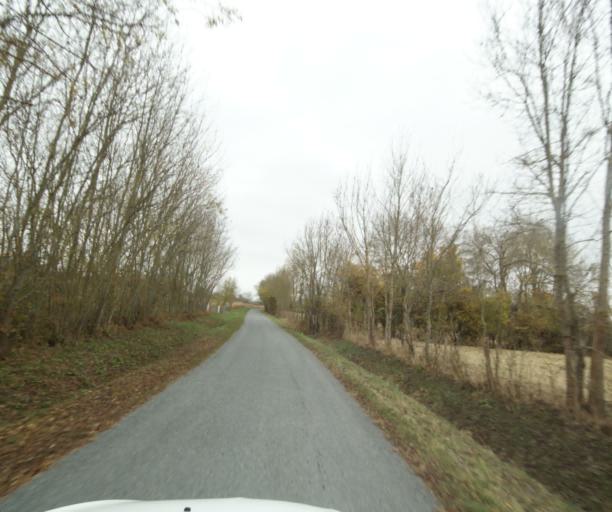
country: FR
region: Poitou-Charentes
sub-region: Departement de la Charente-Maritime
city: Les Gonds
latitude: 45.7297
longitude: -0.6238
